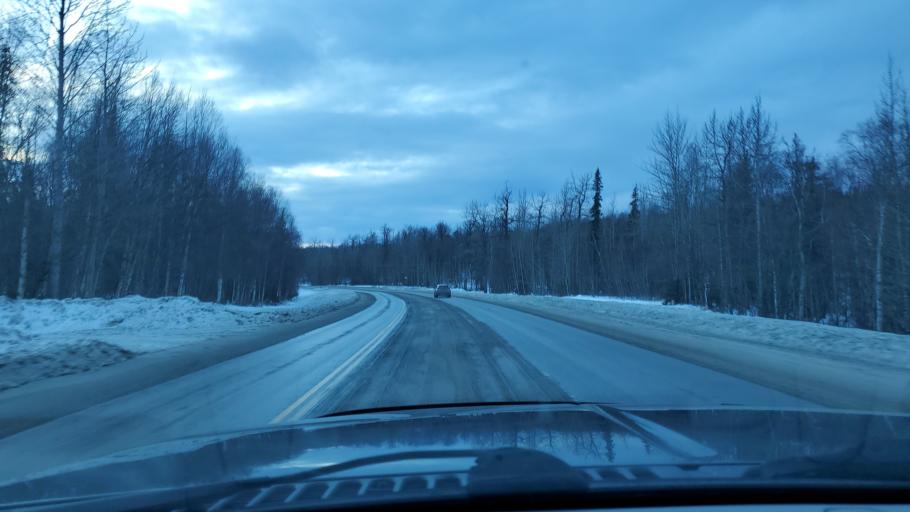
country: US
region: Alaska
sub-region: Matanuska-Susitna Borough
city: Lazy Mountain
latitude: 61.7071
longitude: -148.9449
